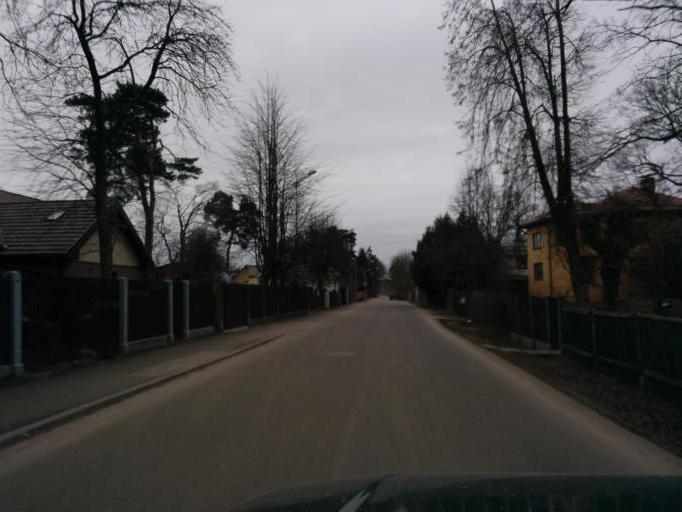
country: LV
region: Jurmala
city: Jurmala
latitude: 56.9648
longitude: 23.8182
